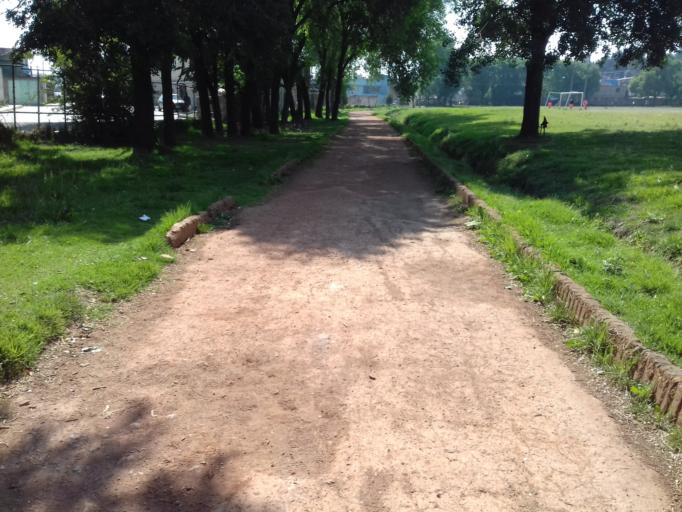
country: MX
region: Mexico
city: San Buenaventura
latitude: 19.2774
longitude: -99.6921
